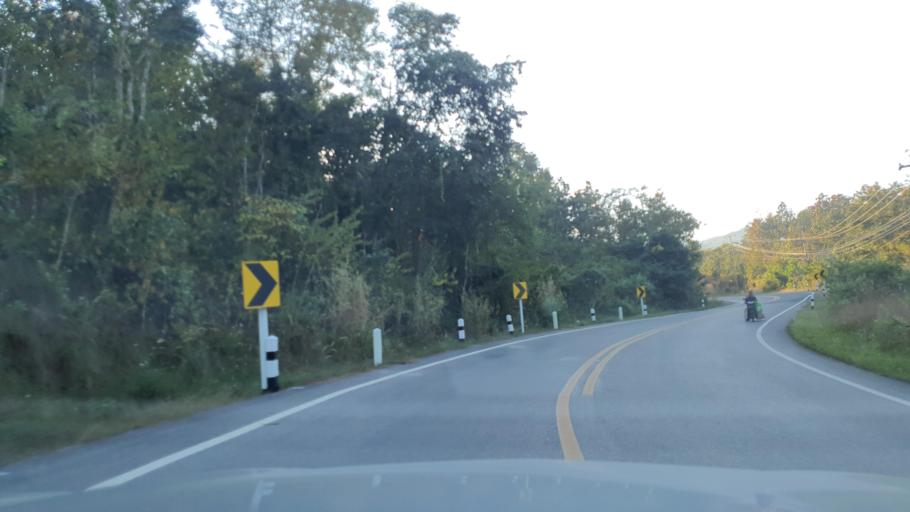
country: TH
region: Phayao
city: Chiang Muan
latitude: 18.9262
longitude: 100.2199
